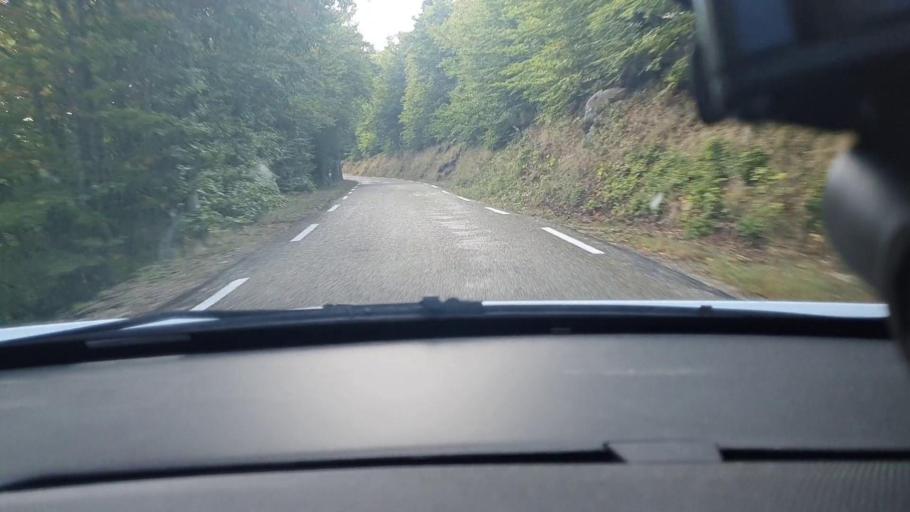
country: FR
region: Languedoc-Roussillon
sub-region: Departement du Gard
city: Branoux-les-Taillades
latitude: 44.3800
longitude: 3.9119
